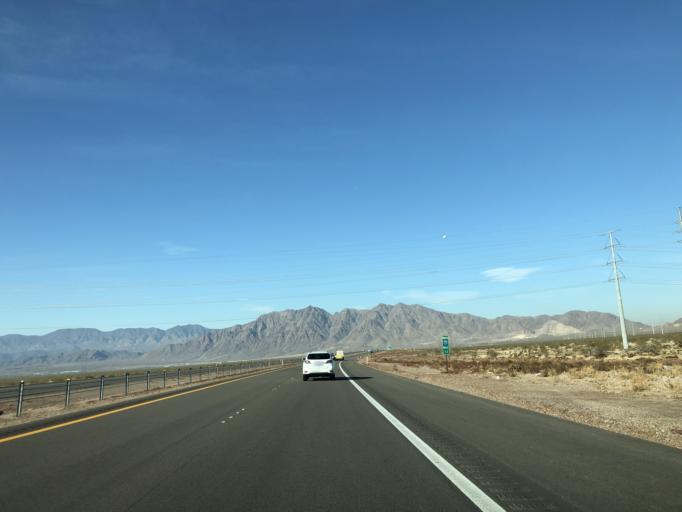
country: US
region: Nevada
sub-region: Clark County
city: Boulder City
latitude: 35.9343
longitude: -114.8604
